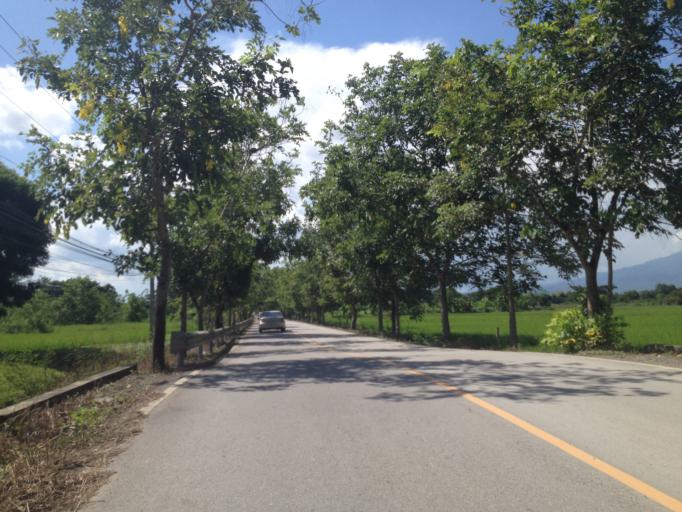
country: TH
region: Chiang Mai
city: Hang Dong
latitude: 18.6822
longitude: 98.9780
